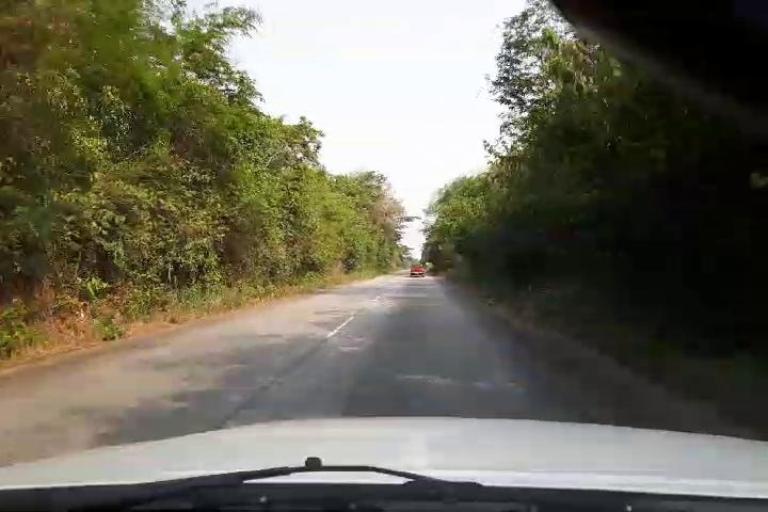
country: SL
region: Southern Province
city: Baiima
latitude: 8.1360
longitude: -11.8909
